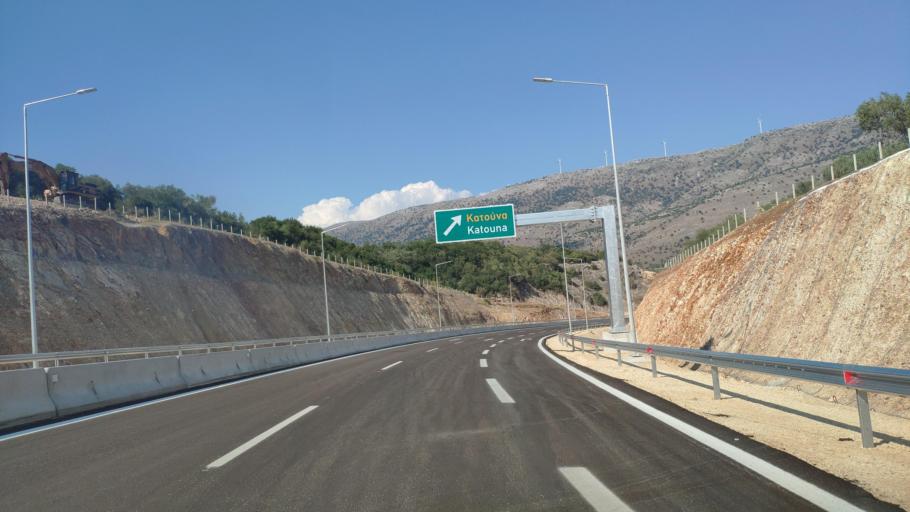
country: GR
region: West Greece
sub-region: Nomos Aitolias kai Akarnanias
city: Stanos
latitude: 38.7764
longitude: 21.1819
